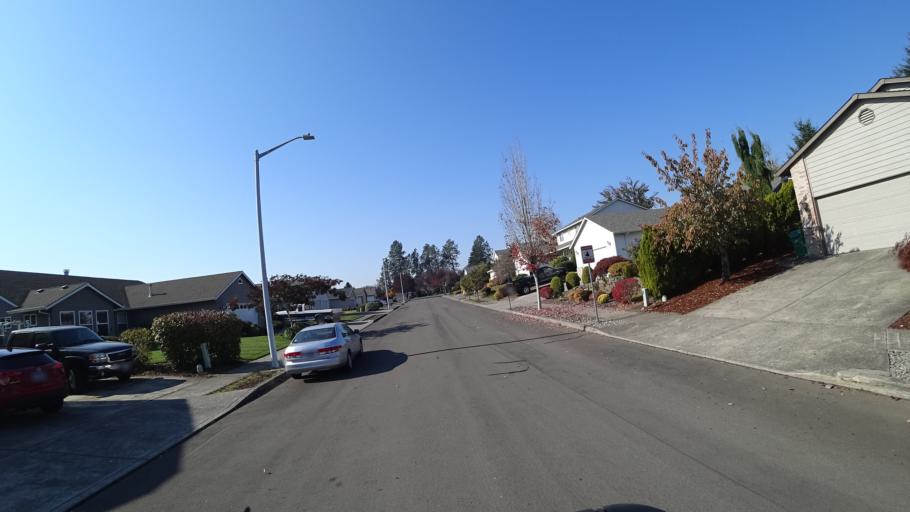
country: US
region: Oregon
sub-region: Multnomah County
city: Gresham
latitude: 45.4946
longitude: -122.4472
